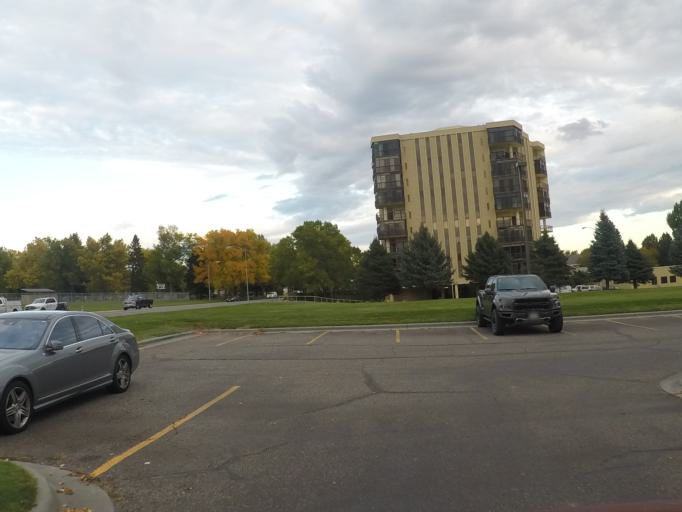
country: US
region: Montana
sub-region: Yellowstone County
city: Billings
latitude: 45.7947
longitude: -108.5523
